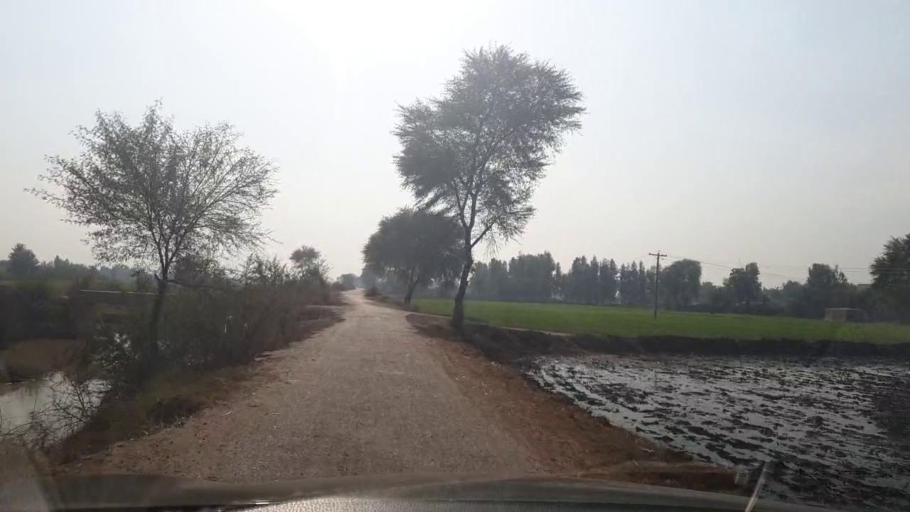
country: PK
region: Sindh
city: Khairpur
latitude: 28.1169
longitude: 69.6407
